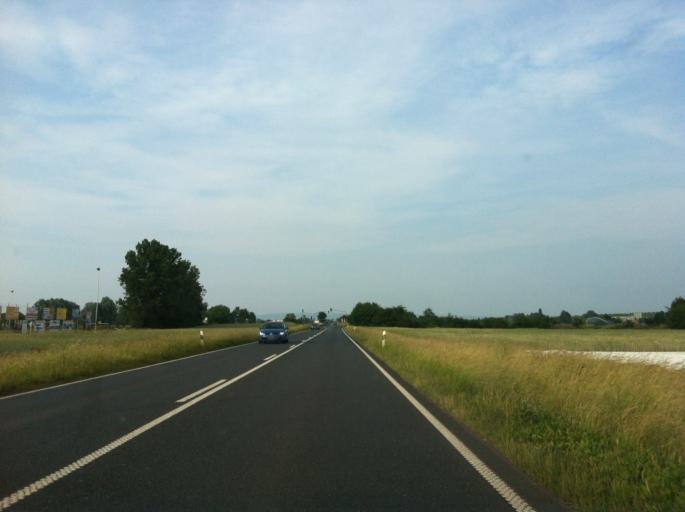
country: DE
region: Hesse
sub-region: Regierungsbezirk Darmstadt
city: Babenhausen
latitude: 49.9420
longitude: 8.9314
